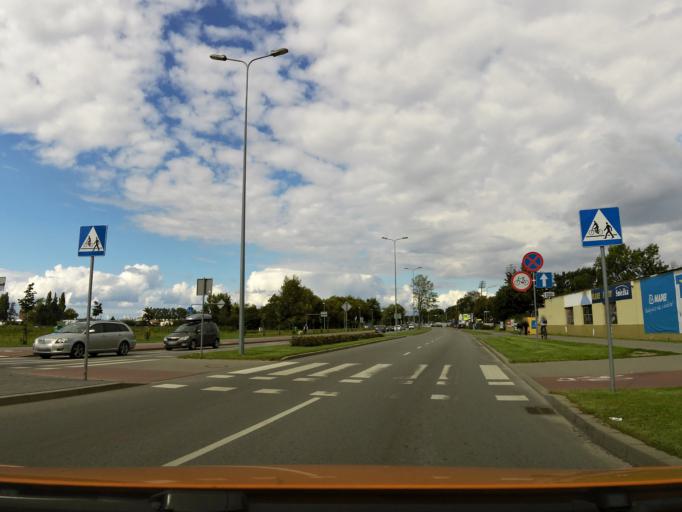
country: PL
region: West Pomeranian Voivodeship
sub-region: Powiat kolobrzeski
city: Kolobrzeg
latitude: 54.1734
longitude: 15.5582
